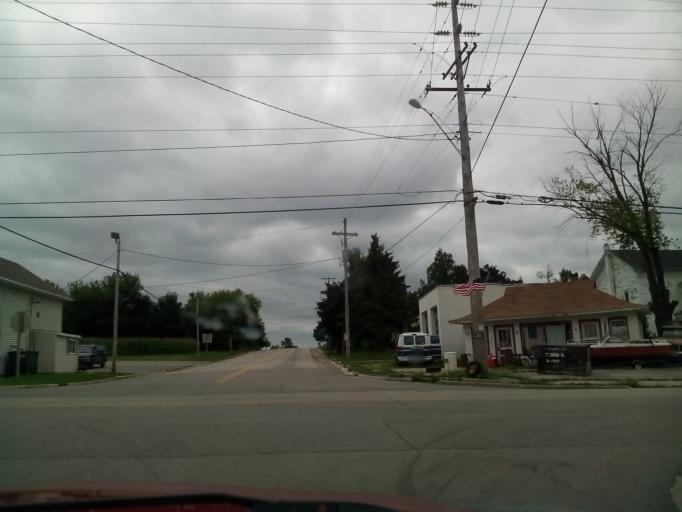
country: US
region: Wisconsin
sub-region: Outagamie County
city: Hortonville
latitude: 44.2727
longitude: -88.6377
